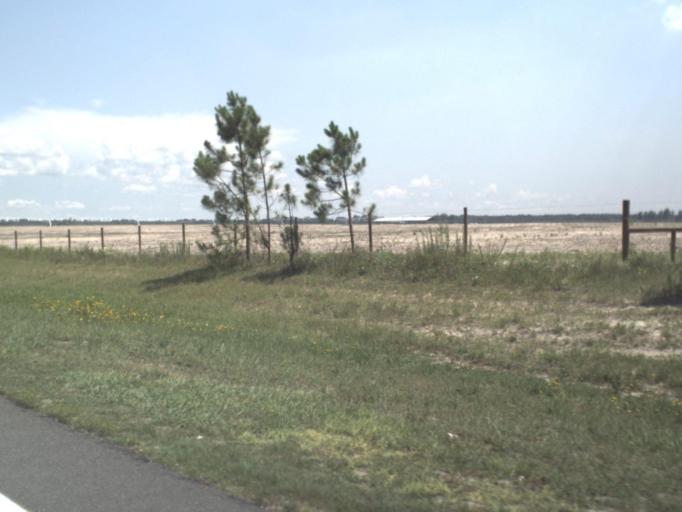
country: US
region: Florida
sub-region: Lafayette County
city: Mayo
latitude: 30.0853
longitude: -83.2224
